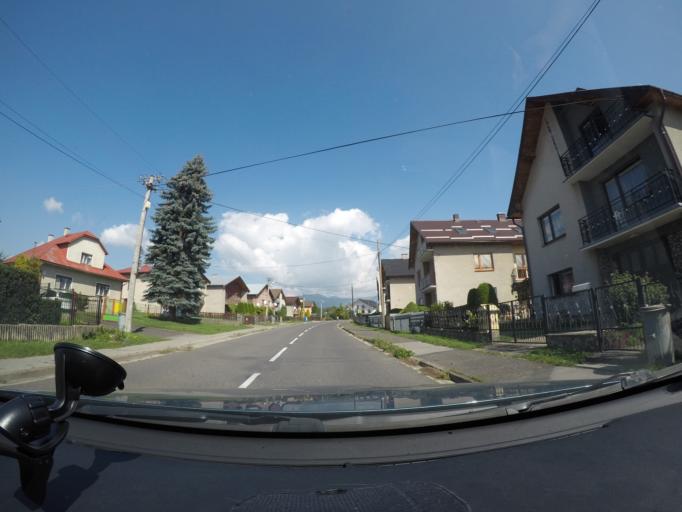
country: SK
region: Zilinsky
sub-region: Okres Liptovsky Mikulas
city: Liptovsky Mikulas
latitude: 49.1012
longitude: 19.5913
